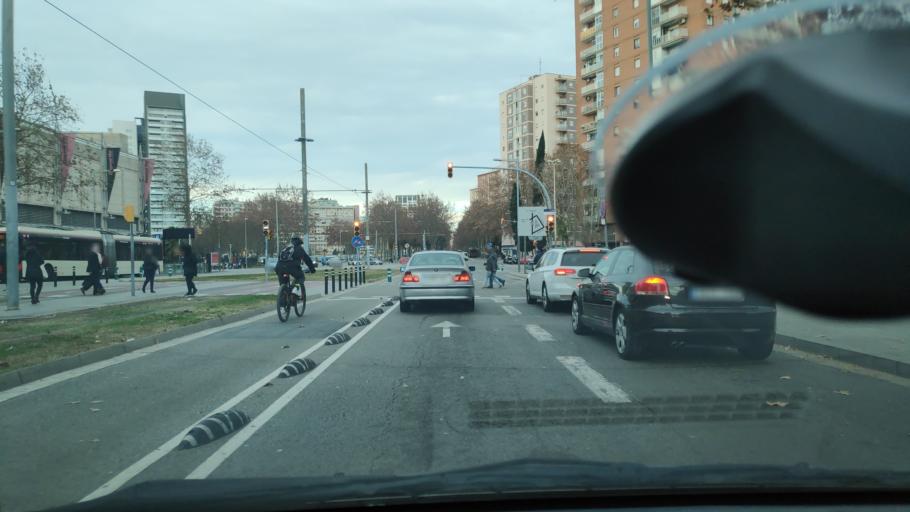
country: ES
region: Catalonia
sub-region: Provincia de Barcelona
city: Sant Marti
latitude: 41.4106
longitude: 2.2155
